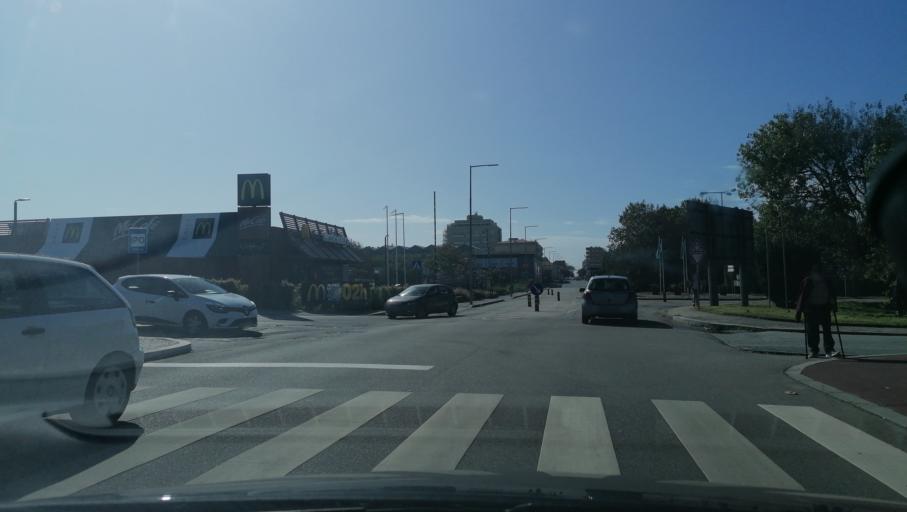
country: PT
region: Aveiro
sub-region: Espinho
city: Espinho
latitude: 41.0159
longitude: -8.6398
